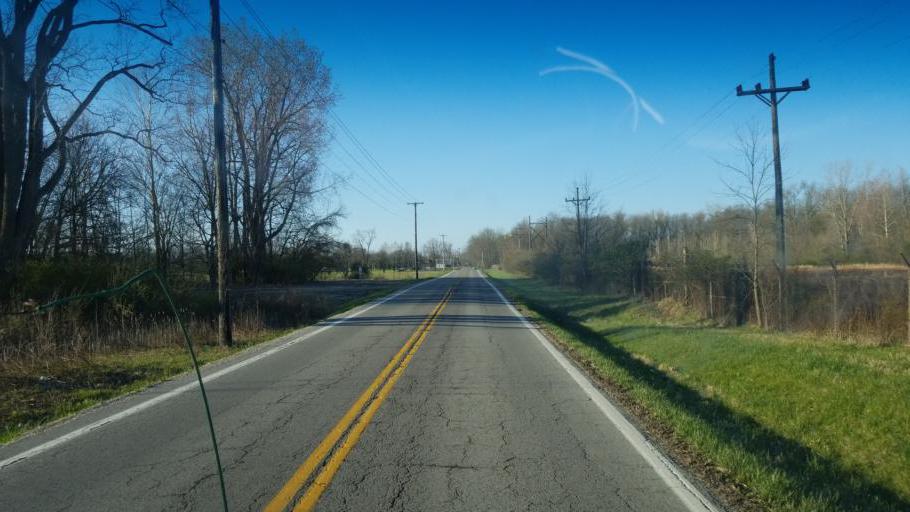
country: US
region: Ohio
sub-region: Marion County
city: Prospect
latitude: 40.4899
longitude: -83.1905
